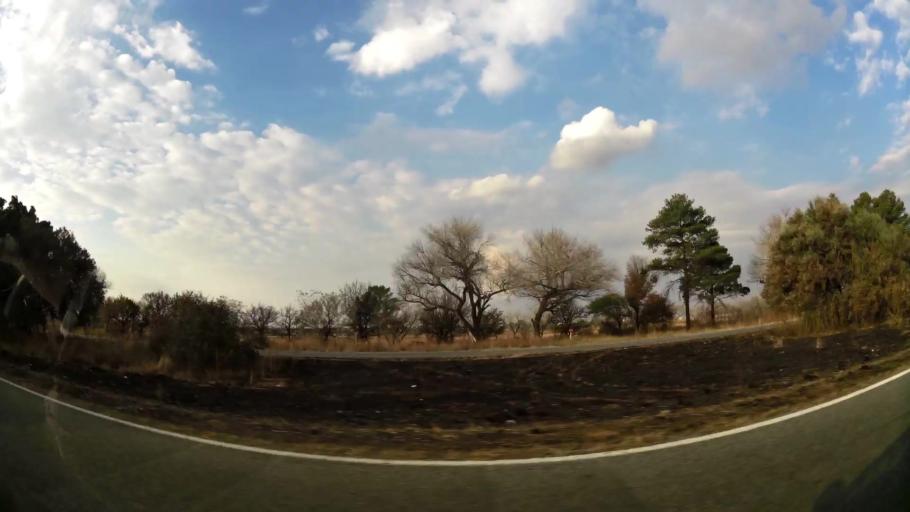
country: ZA
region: Orange Free State
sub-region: Fezile Dabi District Municipality
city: Sasolburg
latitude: -26.7947
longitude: 27.8291
